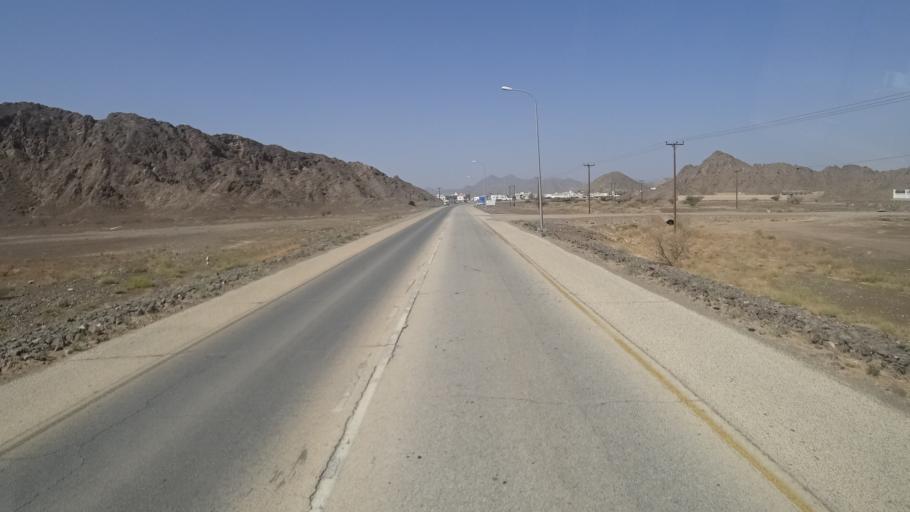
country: OM
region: Ash Sharqiyah
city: Ibra'
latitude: 22.6835
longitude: 58.5608
